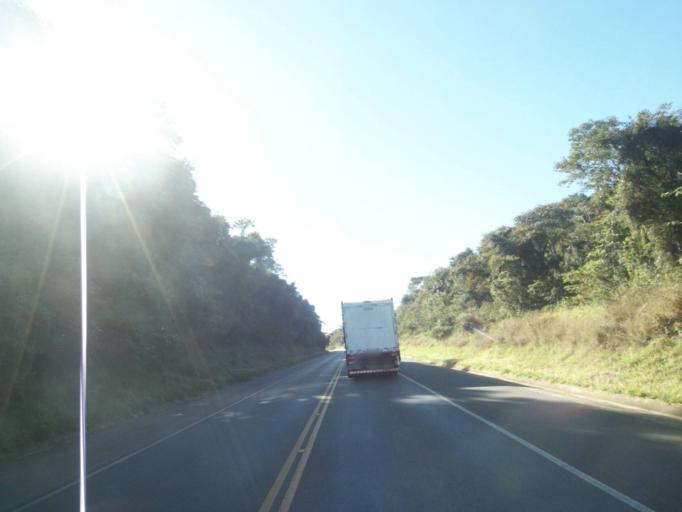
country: BR
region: Parana
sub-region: Tibagi
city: Tibagi
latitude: -24.5610
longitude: -50.4547
